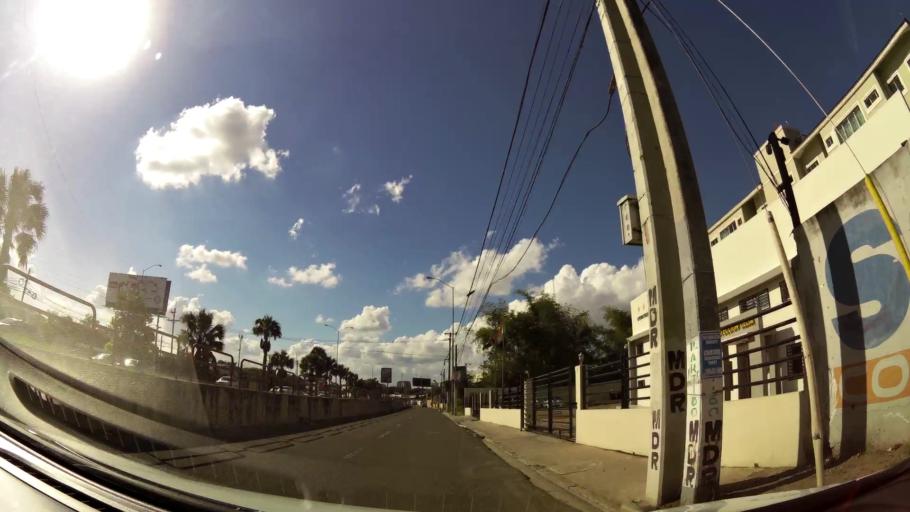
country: DO
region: Santiago
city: Santiago de los Caballeros
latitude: 19.4458
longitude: -70.6728
